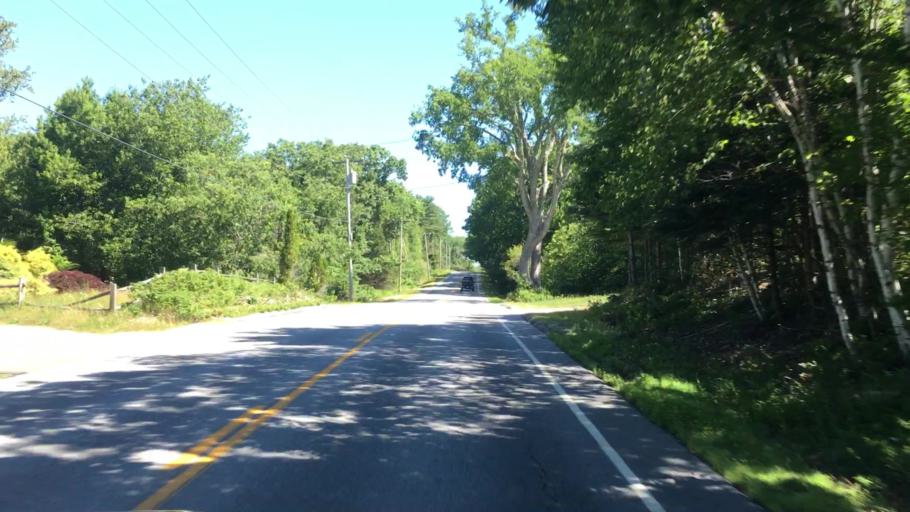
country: US
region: Maine
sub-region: Hancock County
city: Sedgwick
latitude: 44.3543
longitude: -68.6679
